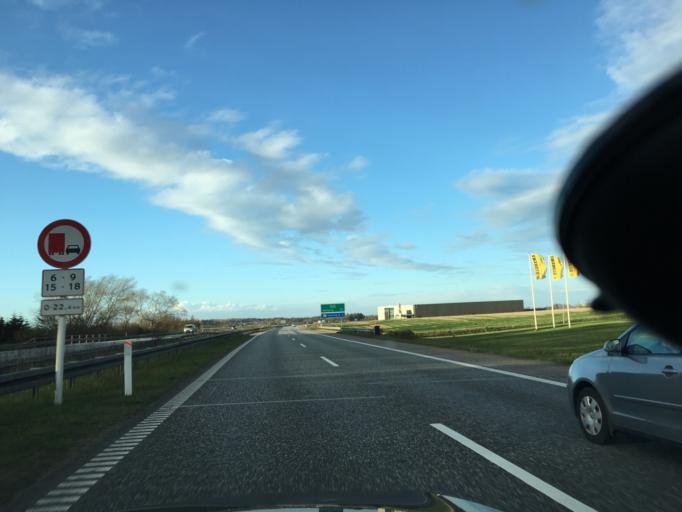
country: DK
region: North Denmark
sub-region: Rebild Kommune
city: Stovring
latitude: 56.8872
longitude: 9.8096
